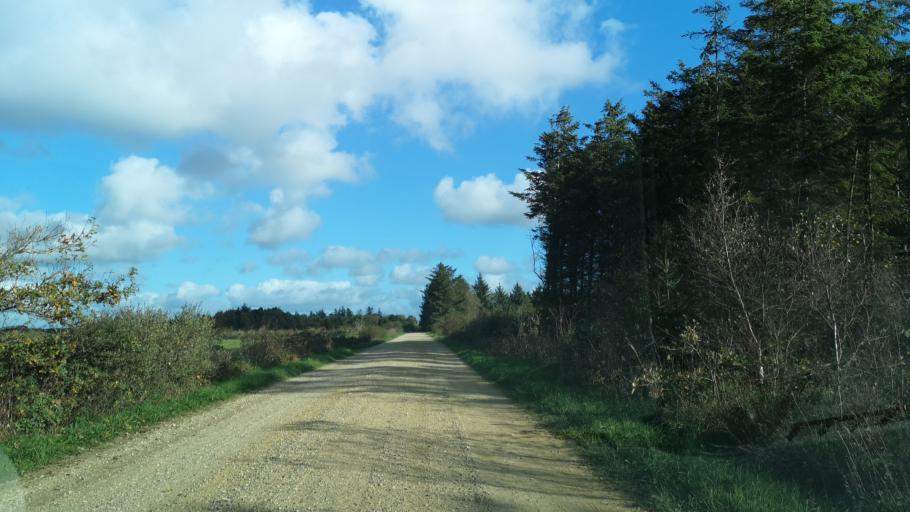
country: DK
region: South Denmark
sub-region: Varde Kommune
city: Oksbol
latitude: 55.6973
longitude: 8.2672
